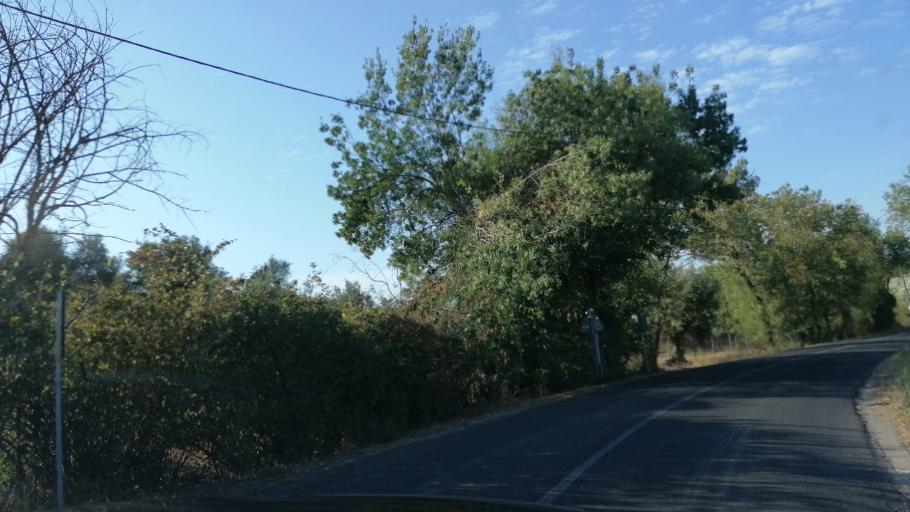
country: PT
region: Santarem
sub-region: Santarem
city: Santarem
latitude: 39.2639
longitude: -8.6652
